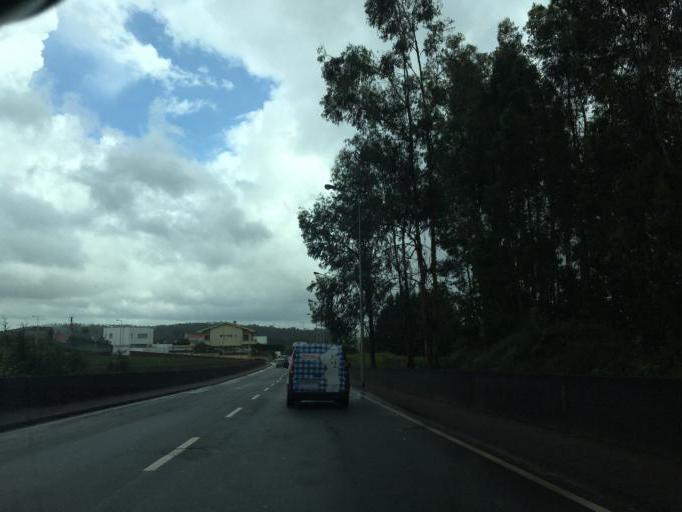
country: PT
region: Porto
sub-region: Maia
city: Nogueira
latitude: 41.2548
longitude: -8.5944
